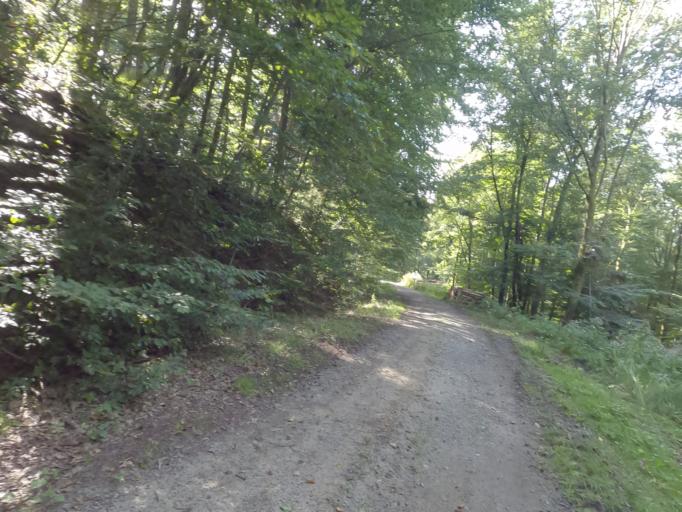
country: DE
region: Bavaria
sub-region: Lower Bavaria
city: Niederalteich
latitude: 48.8147
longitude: 13.0107
